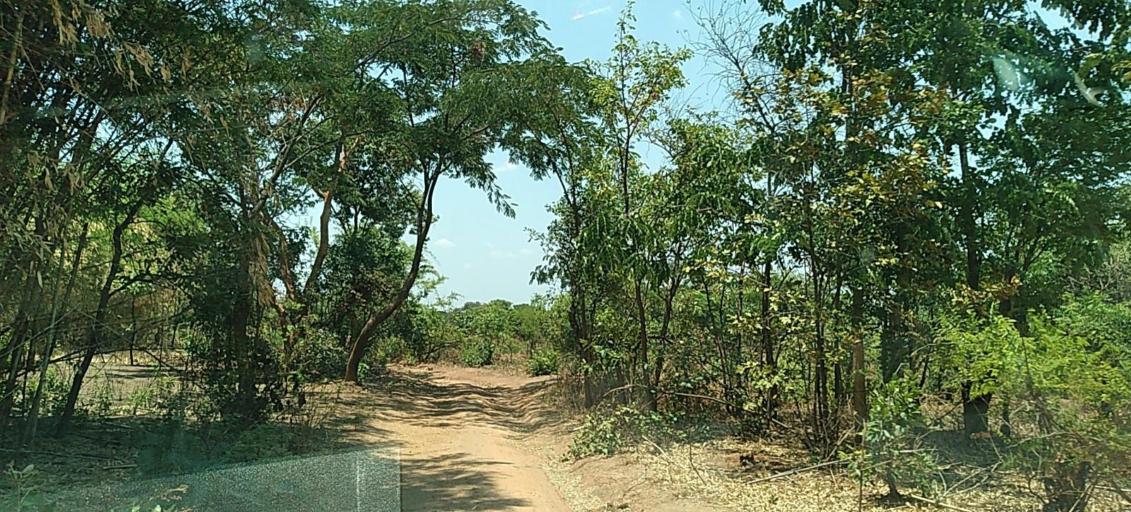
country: ZM
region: Copperbelt
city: Luanshya
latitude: -13.0663
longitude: 28.4048
